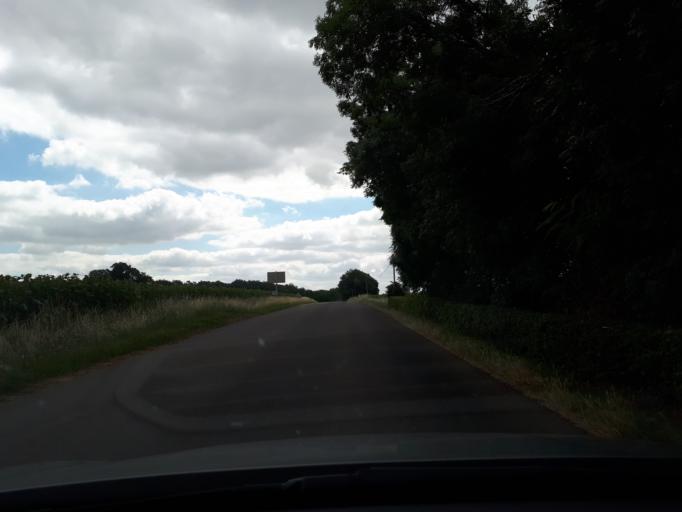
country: FR
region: Midi-Pyrenees
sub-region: Departement du Gers
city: Lectoure
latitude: 43.9329
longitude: 0.5559
